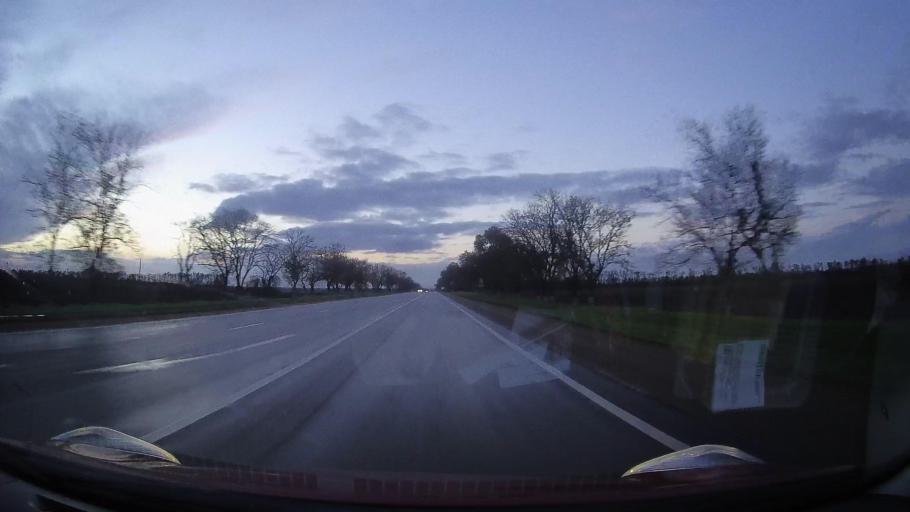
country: RU
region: Krasnodarskiy
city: Zavetnyy
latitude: 44.8906
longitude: 41.2070
